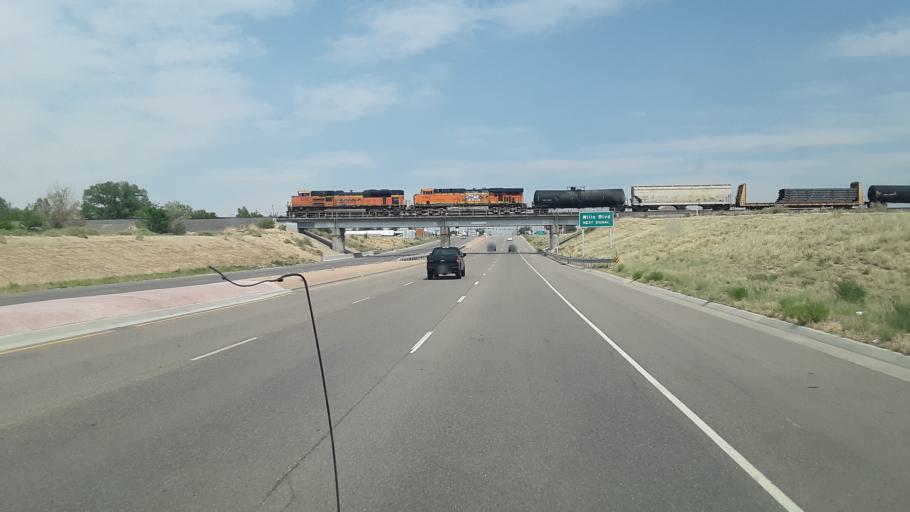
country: US
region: Colorado
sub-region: Pueblo County
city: Pueblo
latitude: 38.3121
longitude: -104.6489
